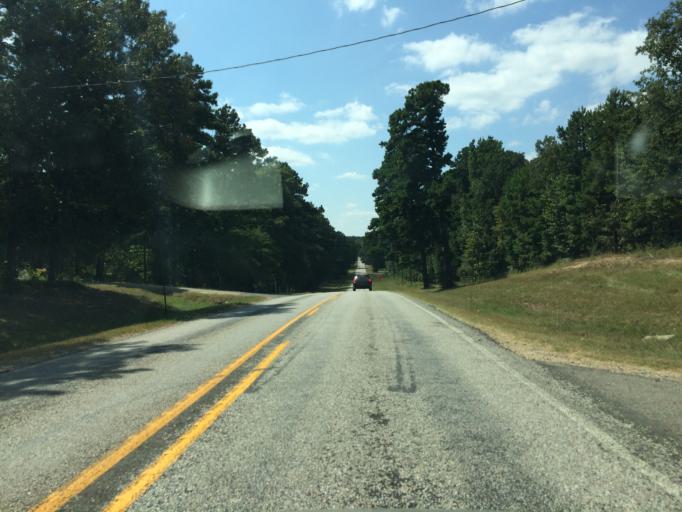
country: US
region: Texas
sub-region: Wood County
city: Hawkins
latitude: 32.6415
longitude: -95.2514
